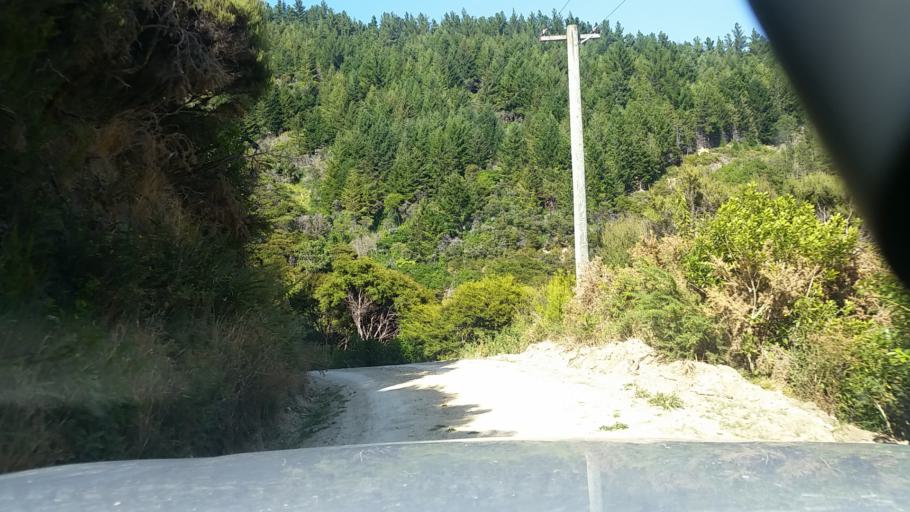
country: NZ
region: Marlborough
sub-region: Marlborough District
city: Picton
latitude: -41.3142
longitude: 174.1750
